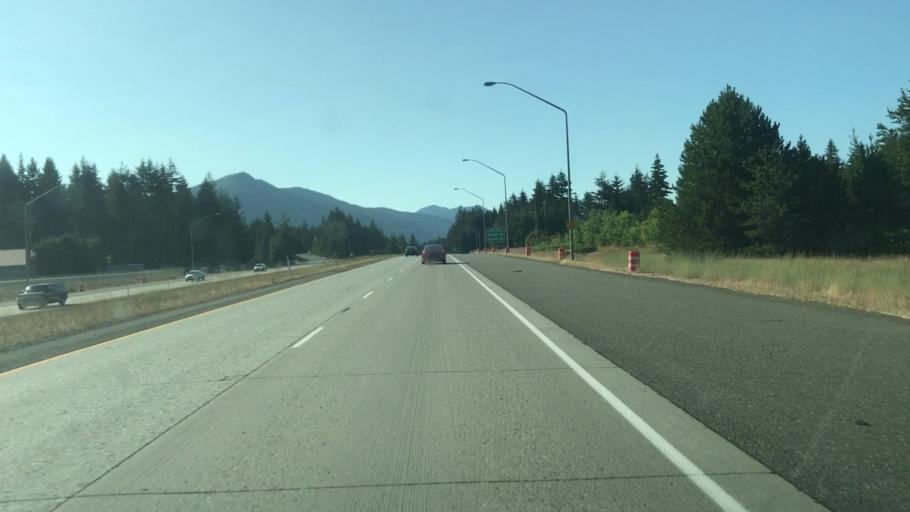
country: US
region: Washington
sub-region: Kittitas County
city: Cle Elum
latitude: 47.2455
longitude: -121.1840
